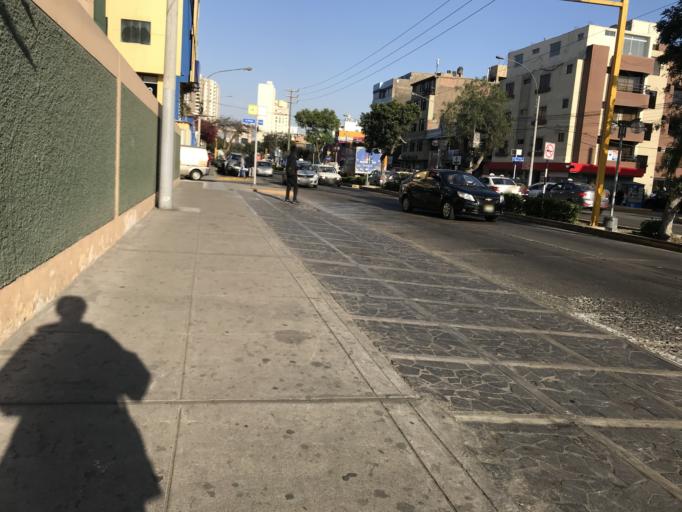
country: PE
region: Callao
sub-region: Callao
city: Callao
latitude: -12.0746
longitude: -77.0832
